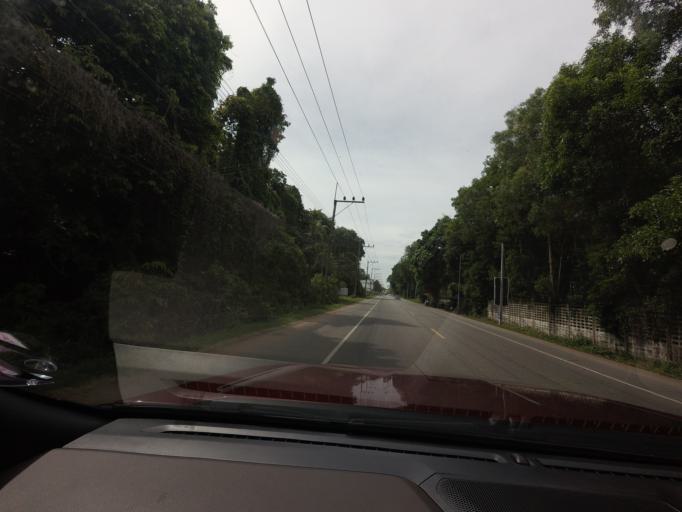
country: TH
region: Narathiwat
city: Tak Bai
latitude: 6.2446
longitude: 102.0741
